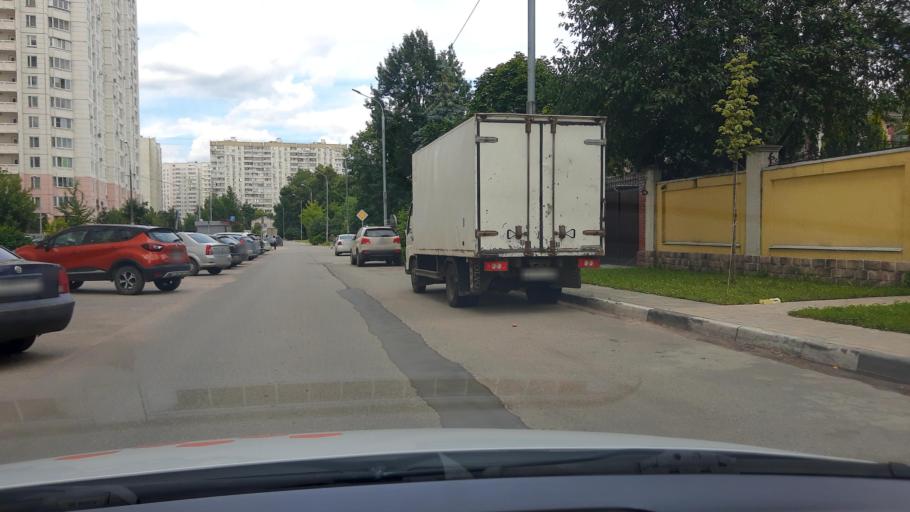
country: RU
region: Moskovskaya
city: Zheleznodorozhnyy
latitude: 55.7434
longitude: 37.9860
